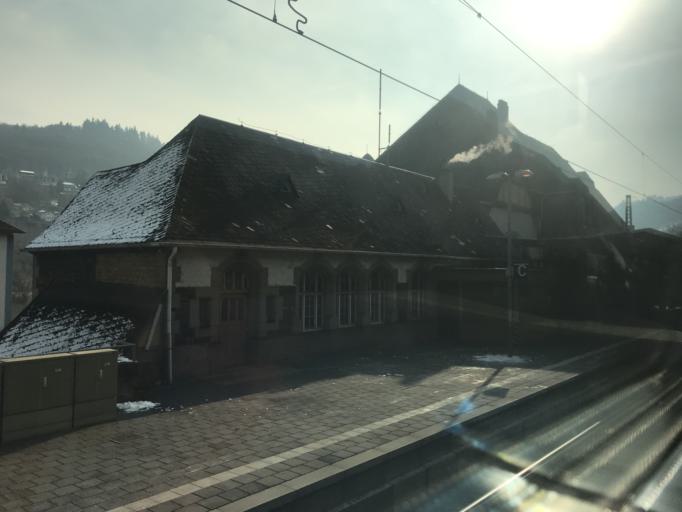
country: DE
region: Rheinland-Pfalz
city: Cochem
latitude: 50.1532
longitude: 7.1667
